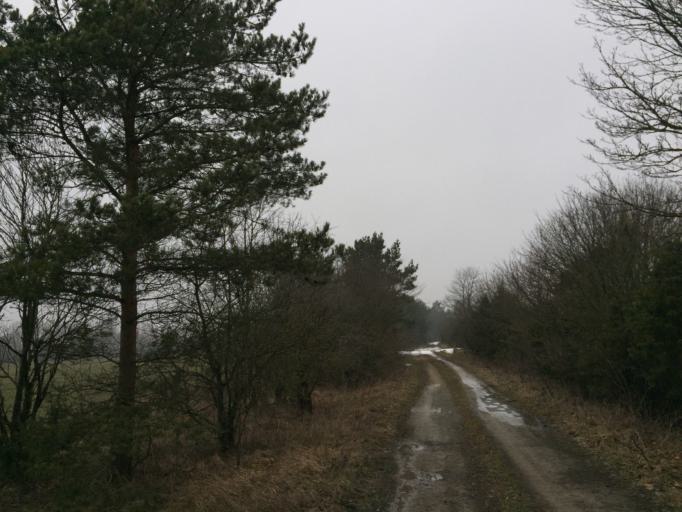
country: EE
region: Saare
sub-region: Orissaare vald
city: Orissaare
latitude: 58.4170
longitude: 22.8230
